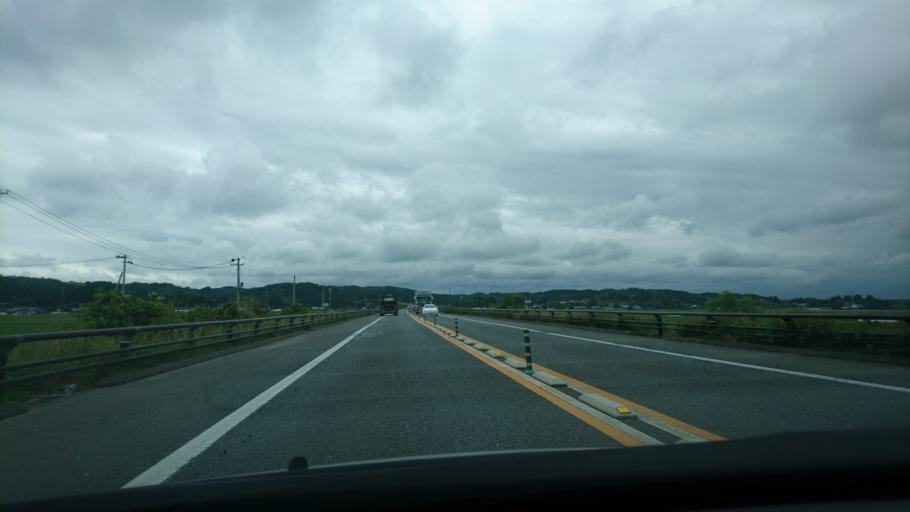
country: JP
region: Miyagi
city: Wakuya
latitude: 38.6606
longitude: 141.2653
